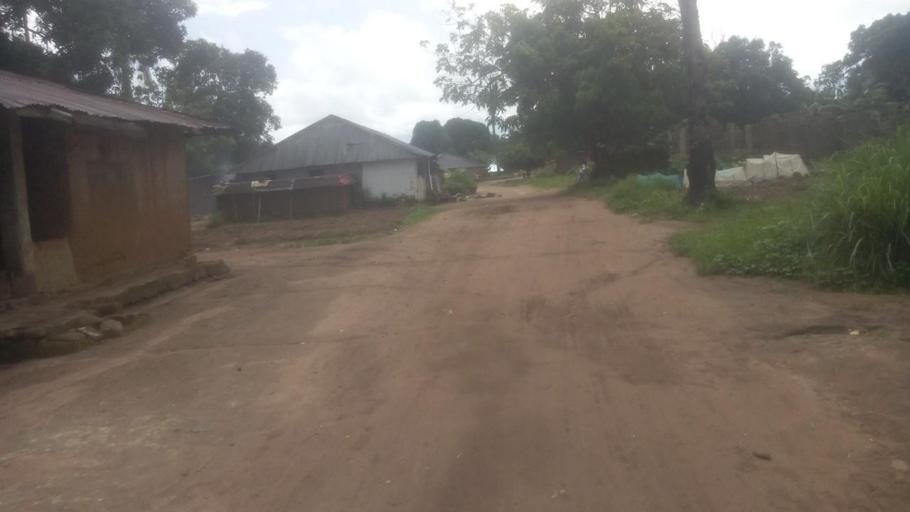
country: SL
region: Northern Province
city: Tintafor
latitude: 8.6377
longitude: -13.2201
